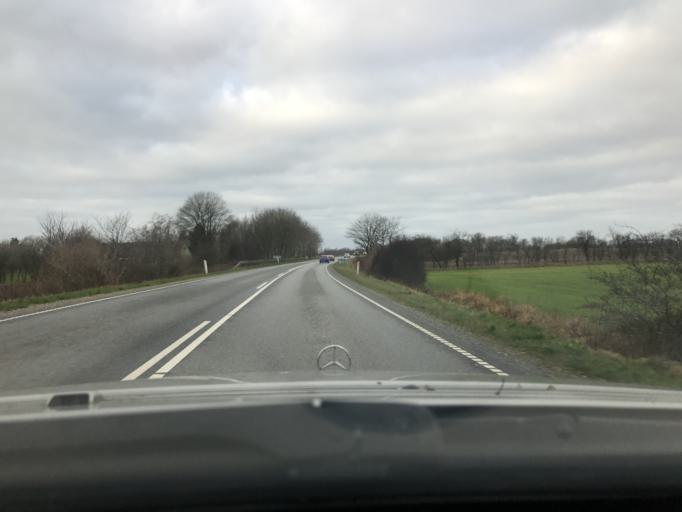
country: DK
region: South Denmark
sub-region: Aabenraa Kommune
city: Rodekro
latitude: 55.0926
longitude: 9.1981
